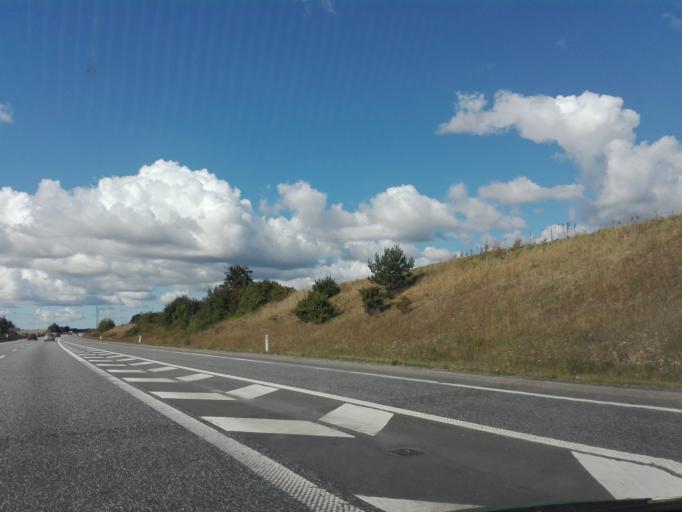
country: DK
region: North Denmark
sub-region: Mariagerfjord Kommune
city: Mariager
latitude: 56.5433
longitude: 9.8956
